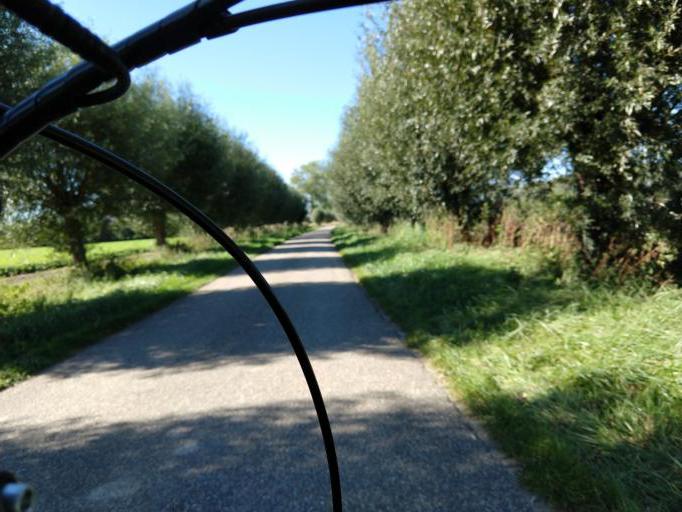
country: NL
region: Zeeland
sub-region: Gemeente Goes
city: Goes
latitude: 51.4410
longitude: 3.8485
